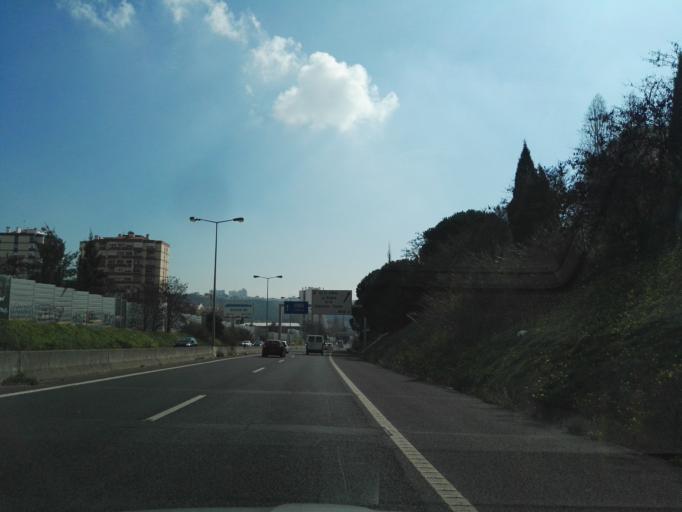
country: PT
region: Lisbon
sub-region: Odivelas
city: Povoa de Santo Adriao
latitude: 38.7982
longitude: -9.1749
